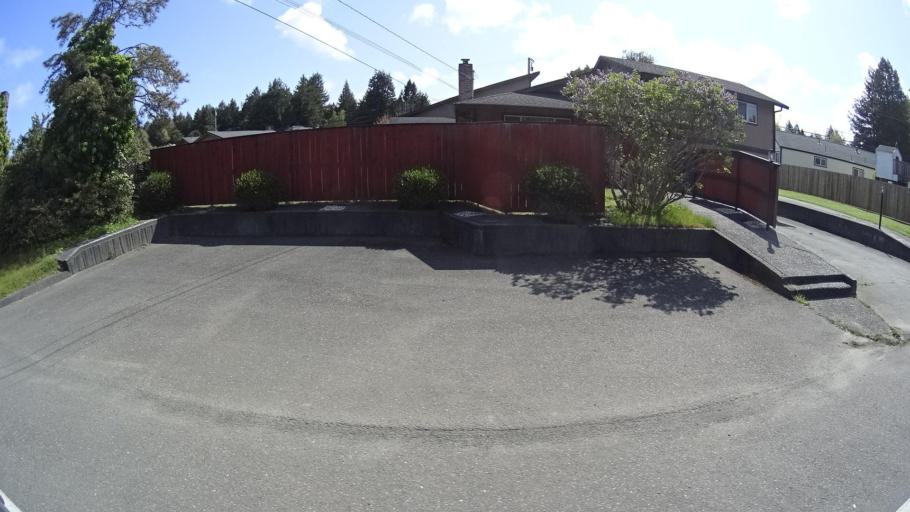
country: US
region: California
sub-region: Humboldt County
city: Pine Hills
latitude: 40.7457
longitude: -124.1477
